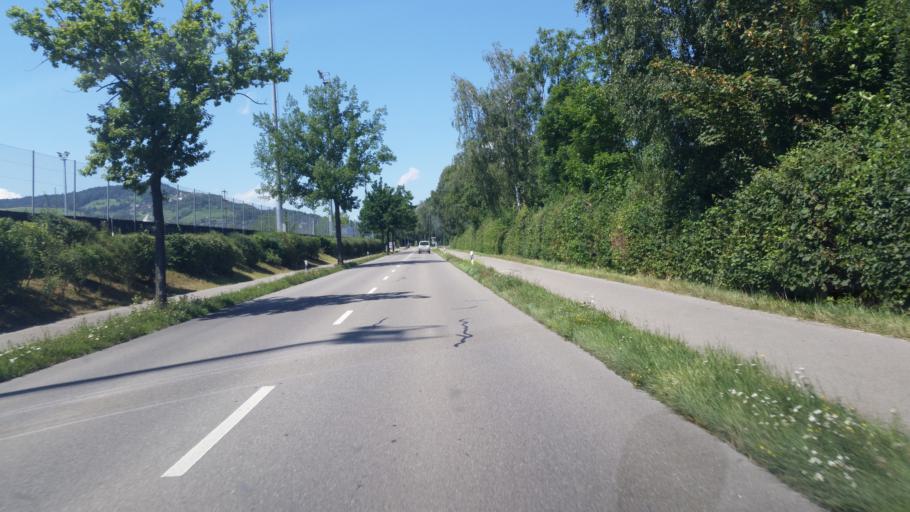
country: CH
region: Zurich
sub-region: Bezirk Dielsdorf
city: Niederhasli
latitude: 47.4826
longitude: 8.4761
